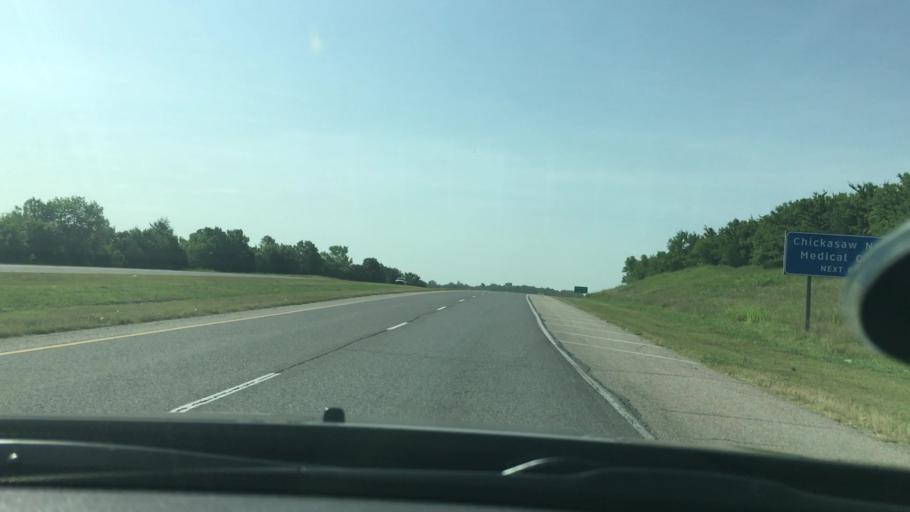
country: US
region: Oklahoma
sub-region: Pontotoc County
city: Ada
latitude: 34.7435
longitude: -96.6496
